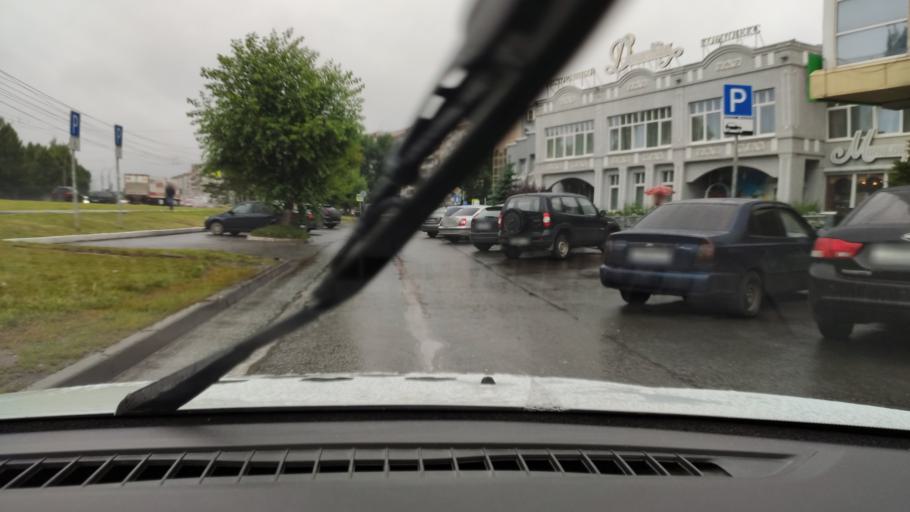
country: RU
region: Udmurtiya
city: Izhevsk
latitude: 56.8788
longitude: 53.2227
